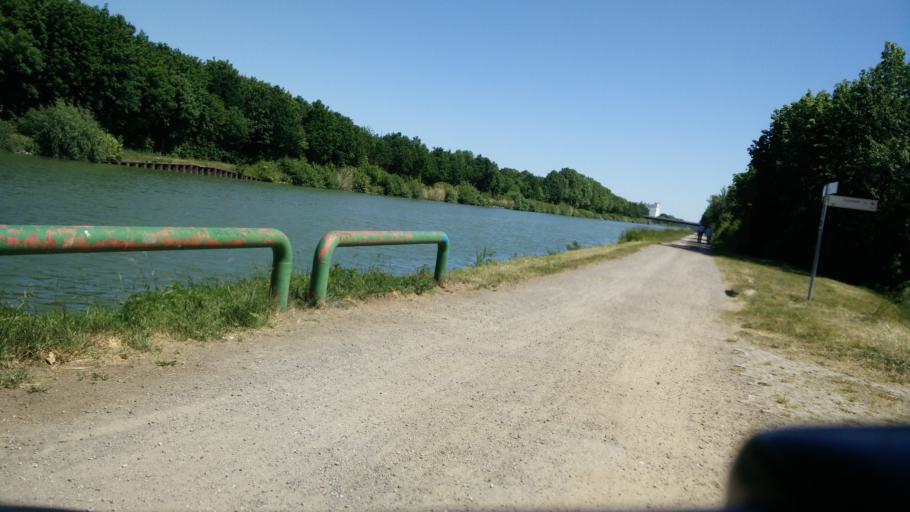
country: DE
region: Lower Saxony
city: Wunstorf
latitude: 52.3977
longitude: 9.4530
